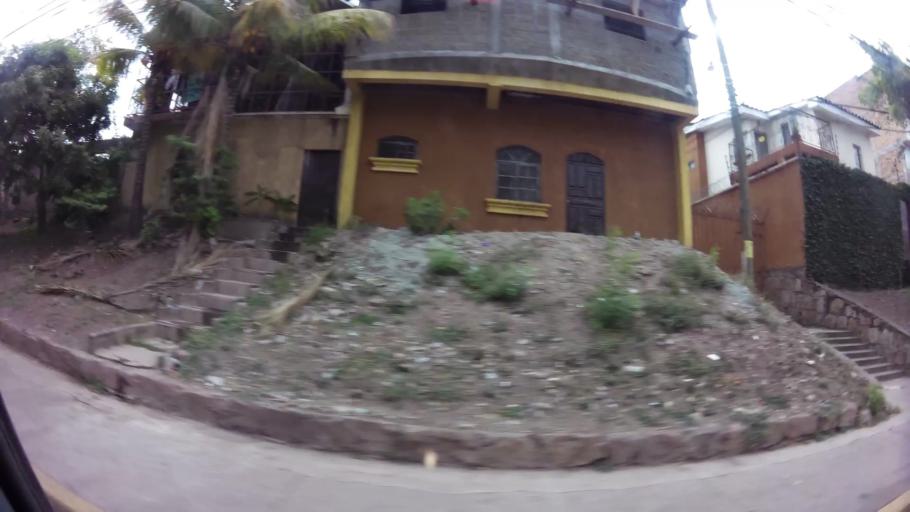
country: HN
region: Francisco Morazan
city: Santa Lucia
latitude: 14.0914
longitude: -87.1618
